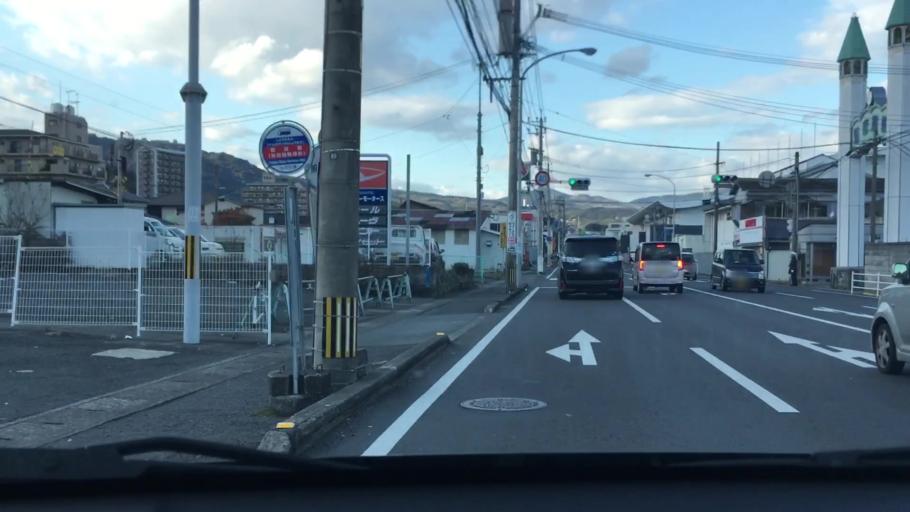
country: JP
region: Oita
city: Beppu
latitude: 33.3207
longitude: 131.4983
